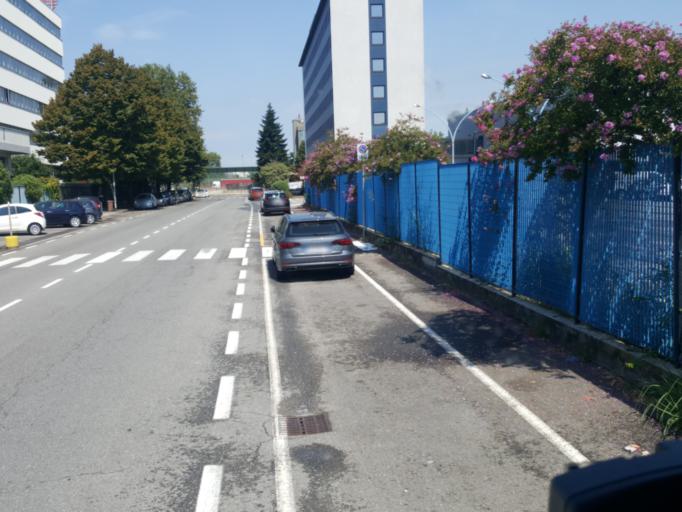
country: IT
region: Lombardy
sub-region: Citta metropolitana di Milano
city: Sesto San Giovanni
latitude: 45.5504
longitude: 9.2442
